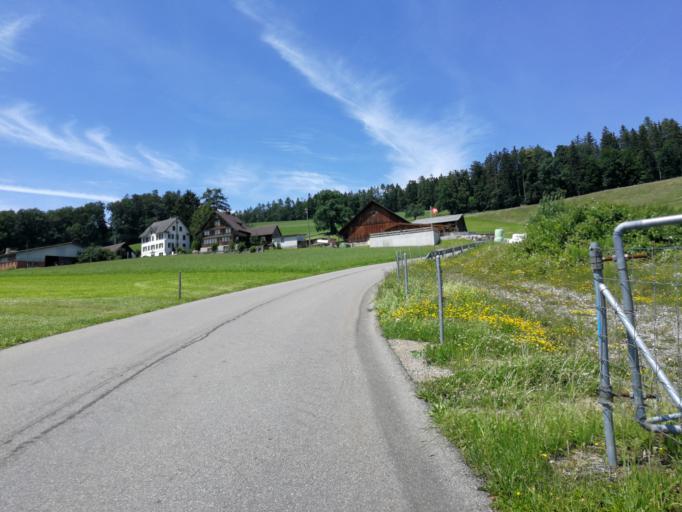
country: CH
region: Schwyz
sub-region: Bezirk March
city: Tuggen
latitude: 47.1994
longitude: 8.9188
